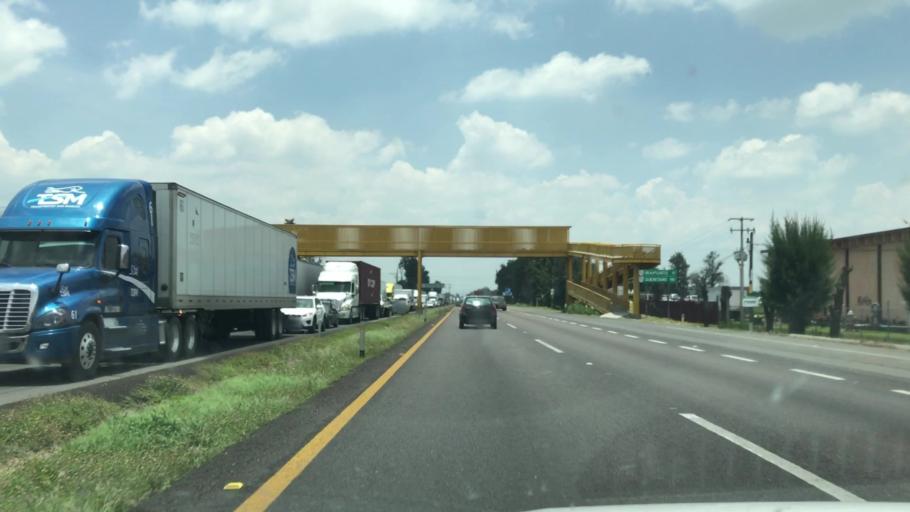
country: MX
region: Guanajuato
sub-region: Irapuato
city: Colonia Morelos de Guadalupe de Rivera
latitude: 20.5970
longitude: -101.4201
